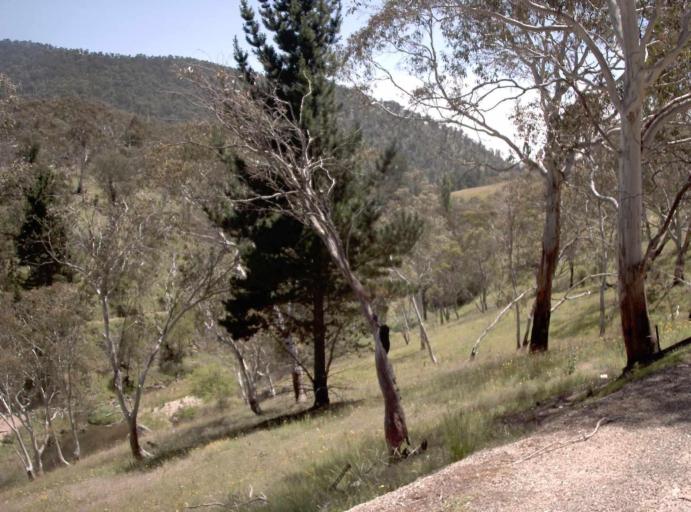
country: AU
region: Victoria
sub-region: Alpine
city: Mount Beauty
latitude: -37.1090
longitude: 147.5780
